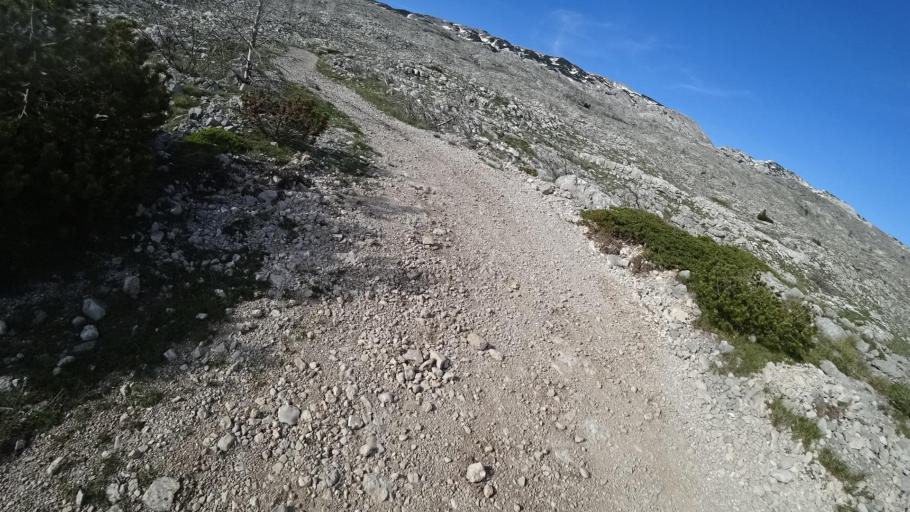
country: BA
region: Federation of Bosnia and Herzegovina
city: Kocerin
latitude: 43.5755
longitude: 17.5404
